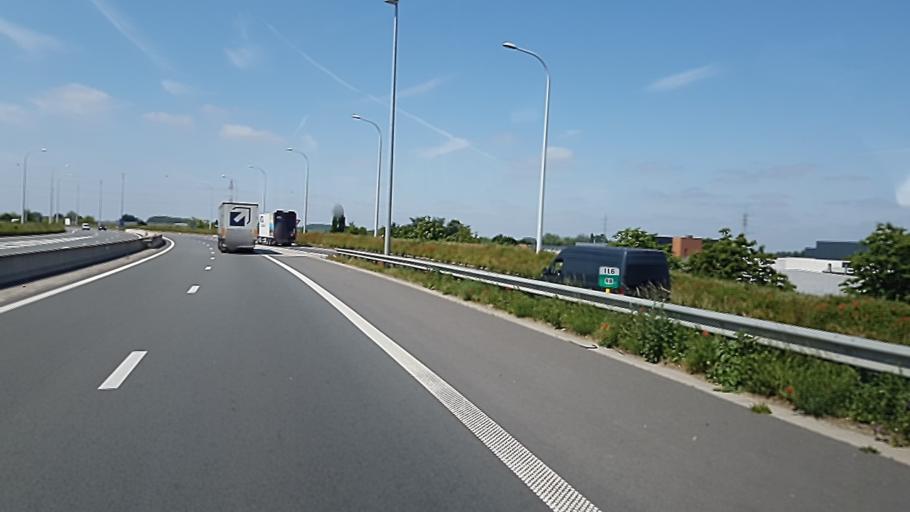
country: BE
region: Flanders
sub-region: Provincie West-Vlaanderen
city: Kortrijk
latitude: 50.8532
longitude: 3.2485
